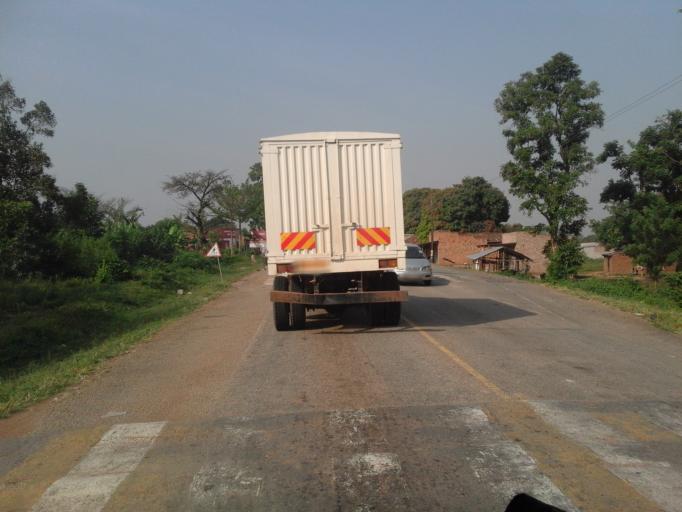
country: UG
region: Eastern Region
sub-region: Budaka District
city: Budaka
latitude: 1.0416
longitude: 34.0264
